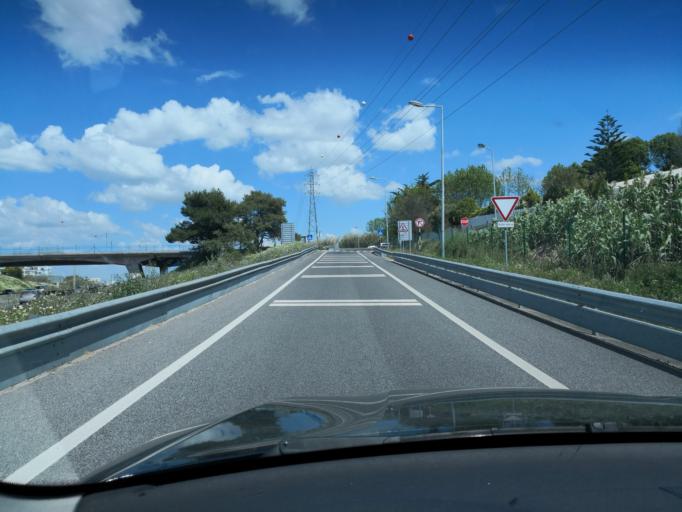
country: PT
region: Setubal
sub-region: Almada
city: Caparica
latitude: 38.6564
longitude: -9.2026
